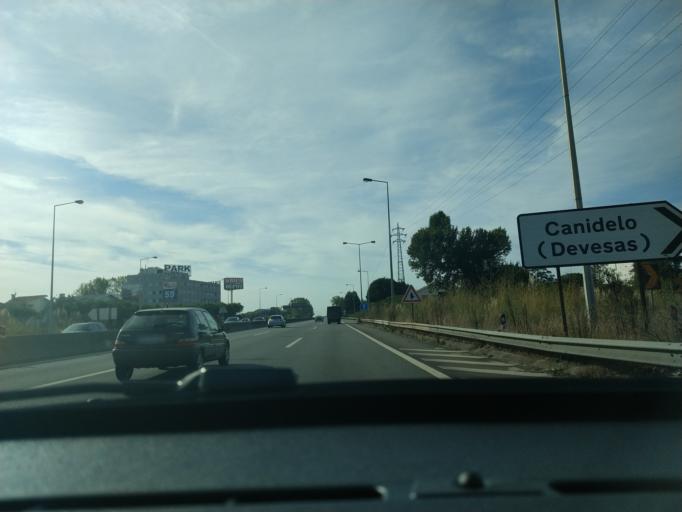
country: PT
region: Porto
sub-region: Vila Nova de Gaia
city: Canidelo
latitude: 41.1282
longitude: -8.6358
